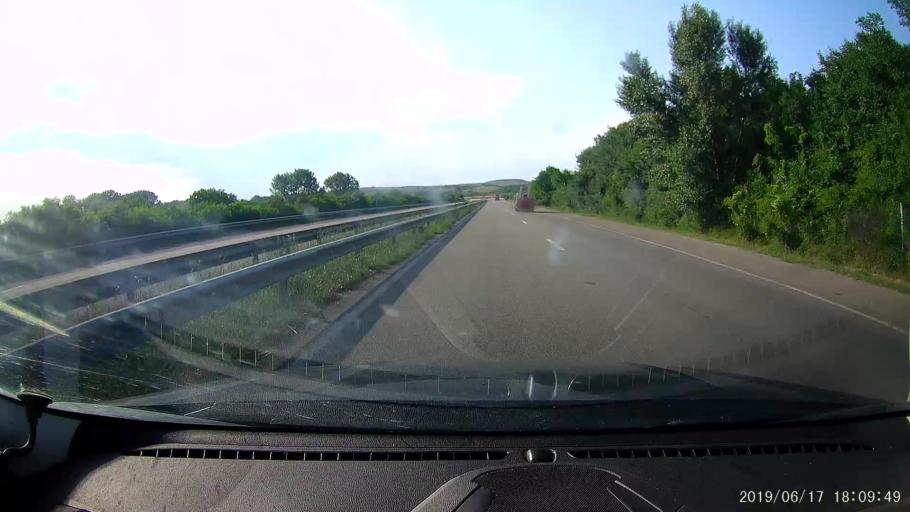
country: BG
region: Khaskovo
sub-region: Obshtina Lyubimets
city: Lyubimets
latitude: 41.8655
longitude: 26.0859
